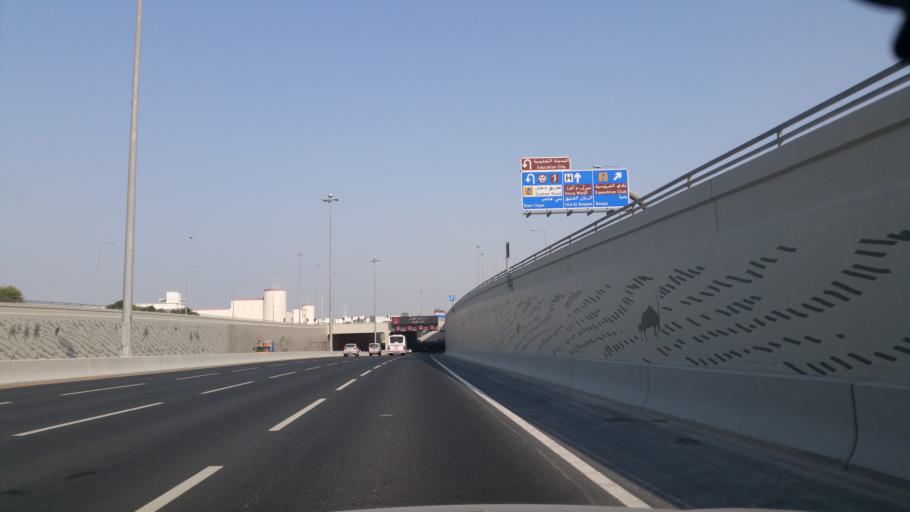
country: QA
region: Baladiyat ar Rayyan
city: Ar Rayyan
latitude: 25.3008
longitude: 51.4273
